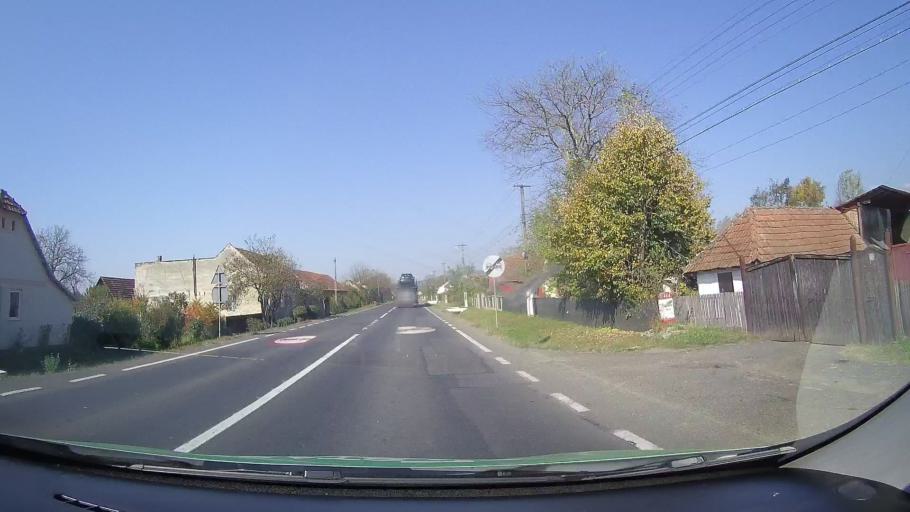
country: RO
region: Arad
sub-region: Comuna Varadia de Mures
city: Varadia de Mures
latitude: 46.0065
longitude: 22.1535
